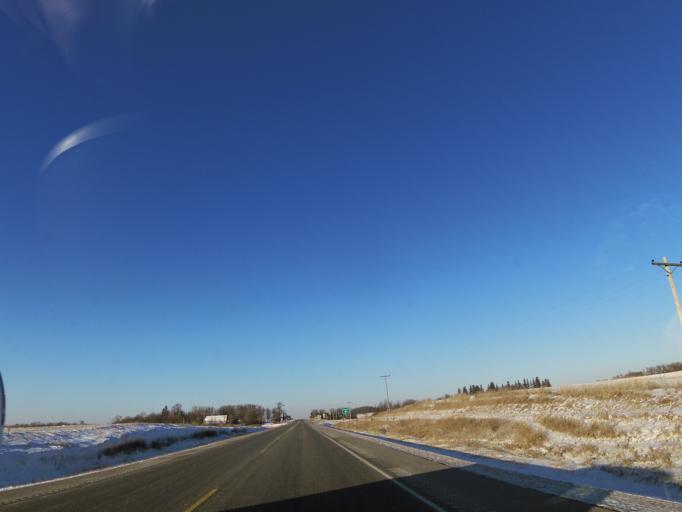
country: US
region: Minnesota
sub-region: Rice County
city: Lonsdale
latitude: 44.5122
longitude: -93.4429
